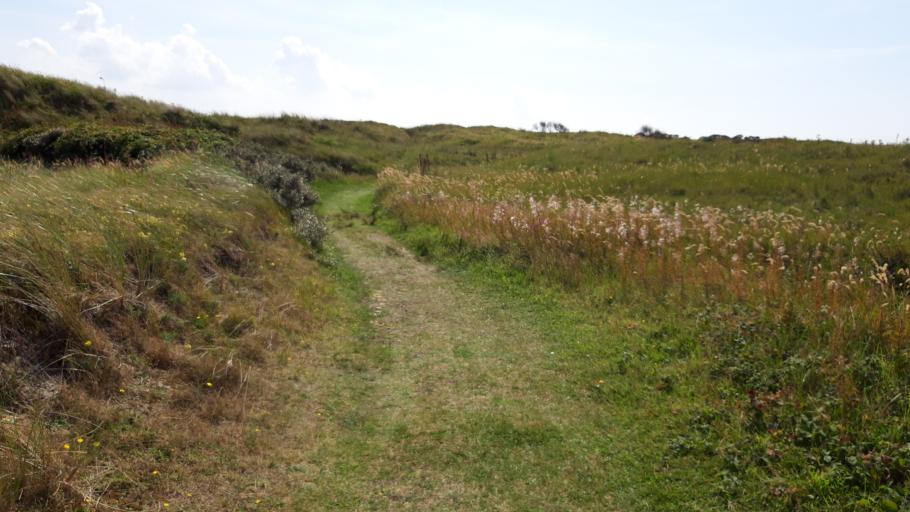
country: NL
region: Friesland
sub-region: Gemeente Ameland
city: Nes
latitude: 53.4622
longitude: 5.8642
